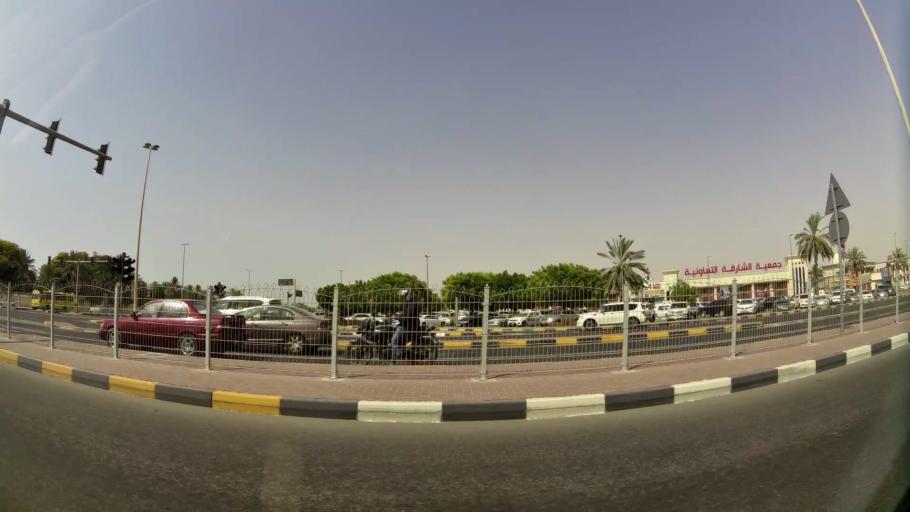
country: AE
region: Ash Shariqah
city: Sharjah
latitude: 25.3457
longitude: 55.4215
